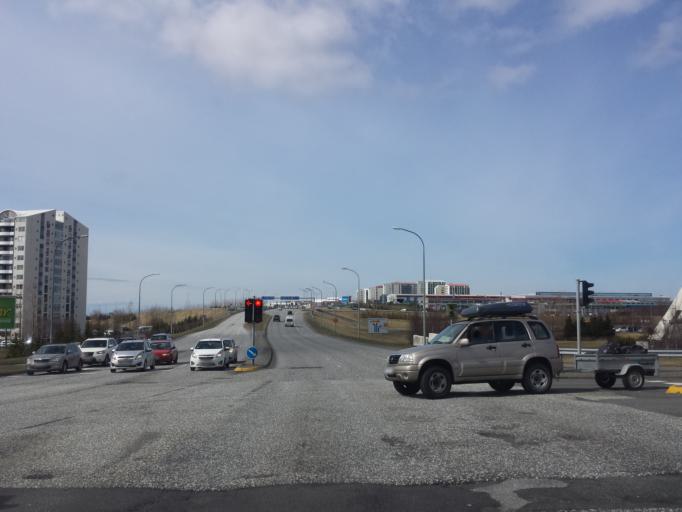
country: IS
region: Capital Region
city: Reykjavik
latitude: 64.1062
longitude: -21.8416
